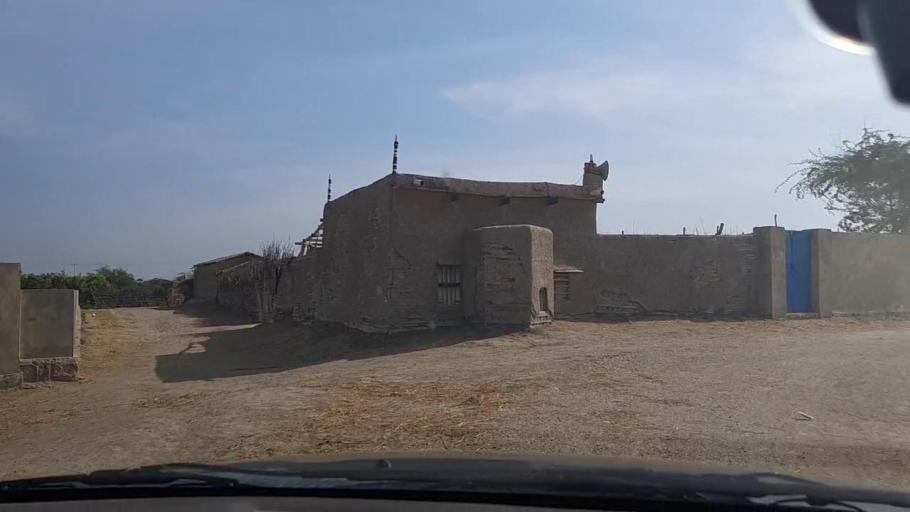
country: PK
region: Sindh
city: Mirpur Batoro
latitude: 24.7447
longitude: 68.2721
